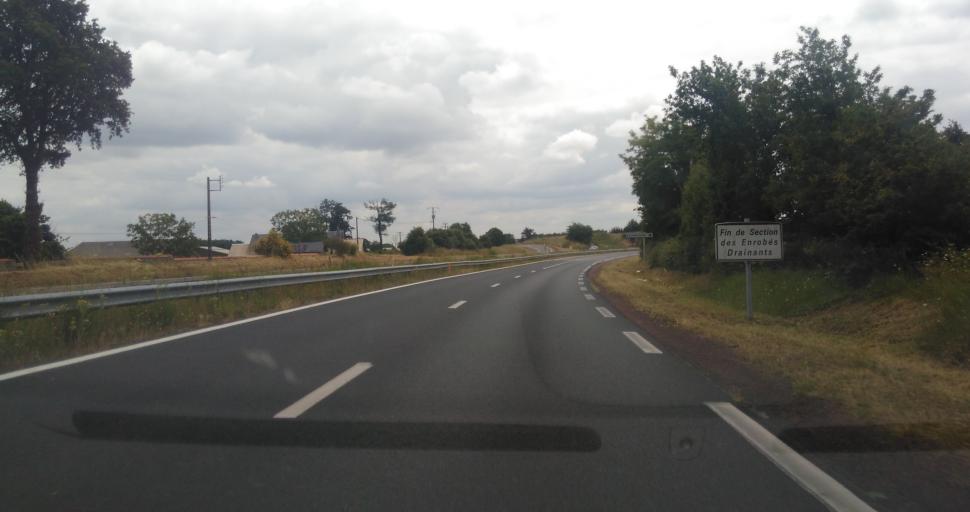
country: FR
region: Pays de la Loire
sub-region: Departement de la Vendee
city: Bournezeau
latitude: 46.6411
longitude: -1.1911
